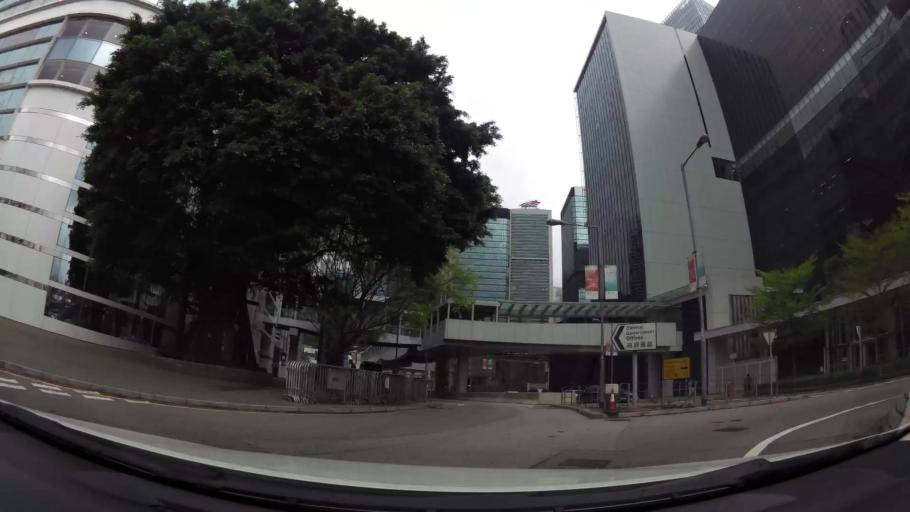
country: HK
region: Wanchai
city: Wan Chai
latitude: 22.2810
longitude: 114.1670
